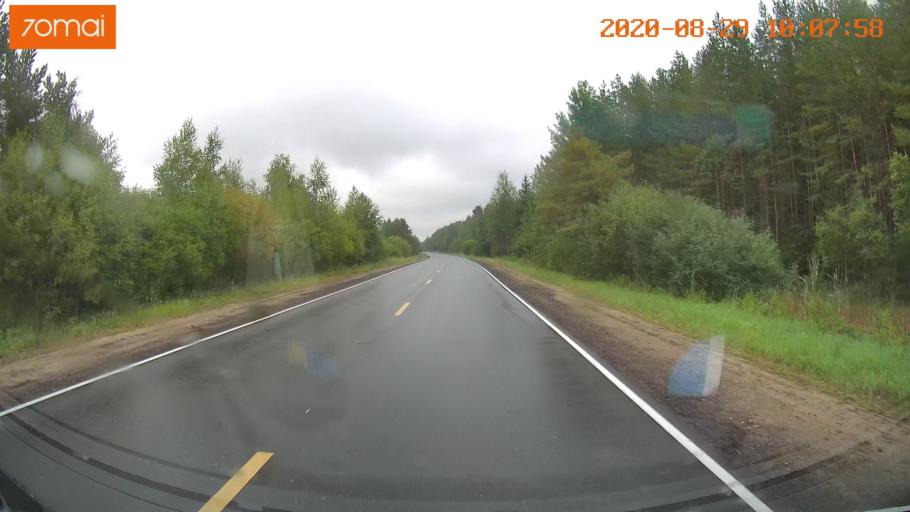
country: RU
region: Ivanovo
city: Kuznechikha
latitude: 57.3776
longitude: 42.5785
